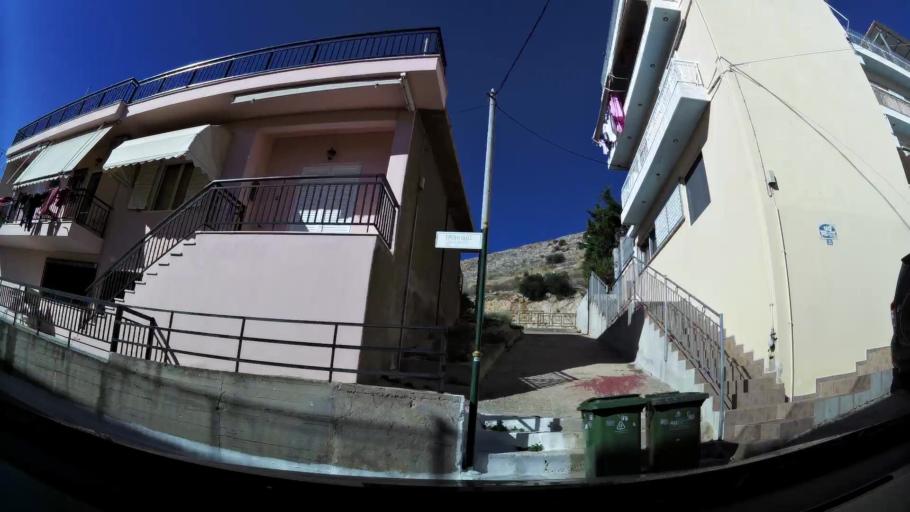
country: GR
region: Attica
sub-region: Nomos Piraios
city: Keratsini
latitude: 37.9660
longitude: 23.6063
